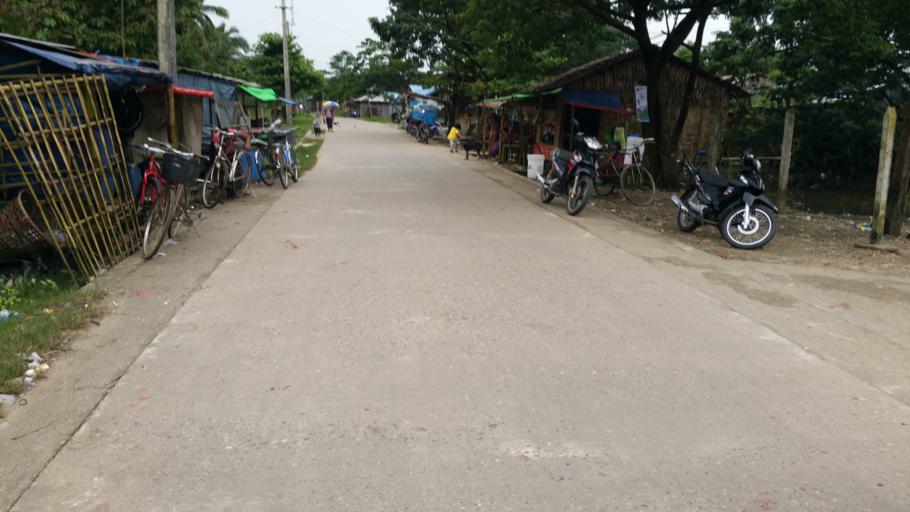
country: MM
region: Yangon
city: Yangon
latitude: 16.7628
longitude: 96.1383
